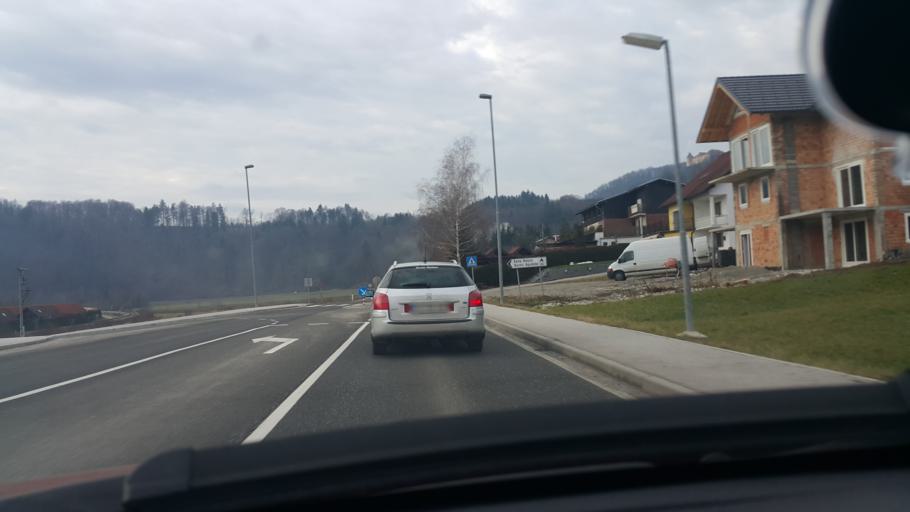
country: SI
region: Podcetrtek
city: Podcetrtek
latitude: 46.1662
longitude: 15.6034
